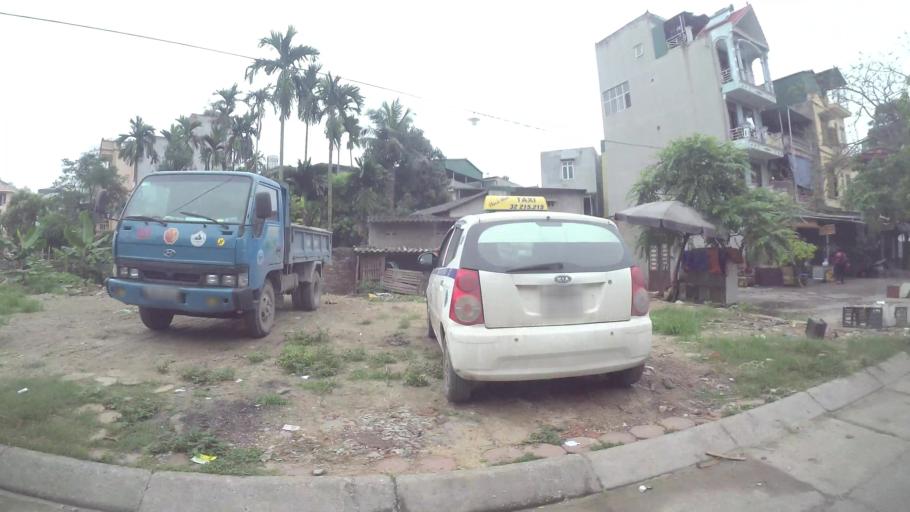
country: VN
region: Ha Noi
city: Hai BaTrung
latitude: 20.9989
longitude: 105.8837
